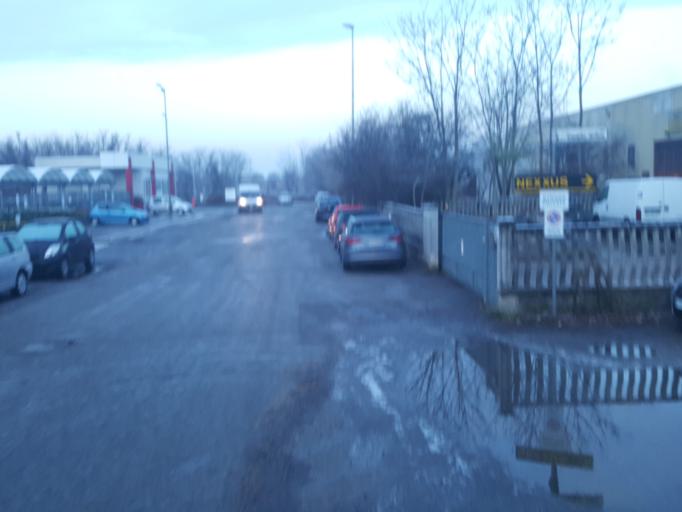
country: IT
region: Lombardy
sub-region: Provincia di Pavia
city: Voghera
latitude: 45.0009
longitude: 8.9865
